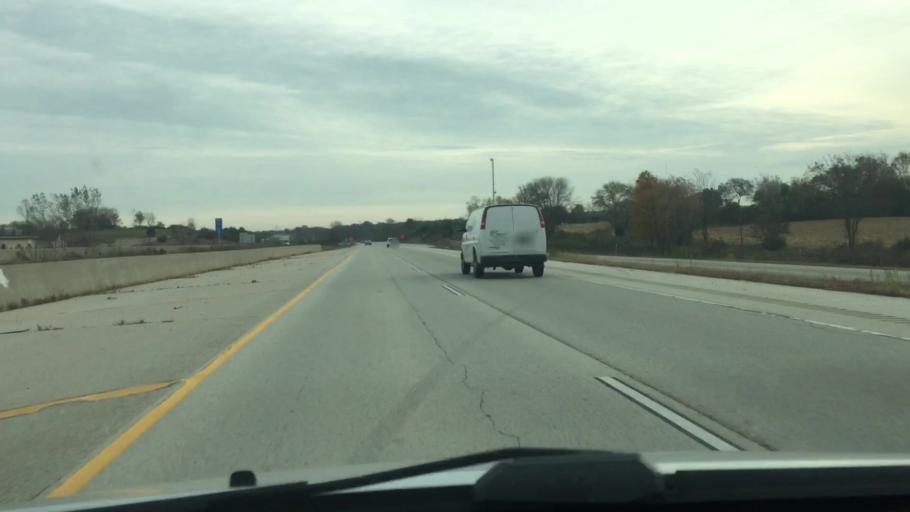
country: US
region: Wisconsin
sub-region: Waukesha County
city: Big Bend
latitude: 42.9114
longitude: -88.2159
